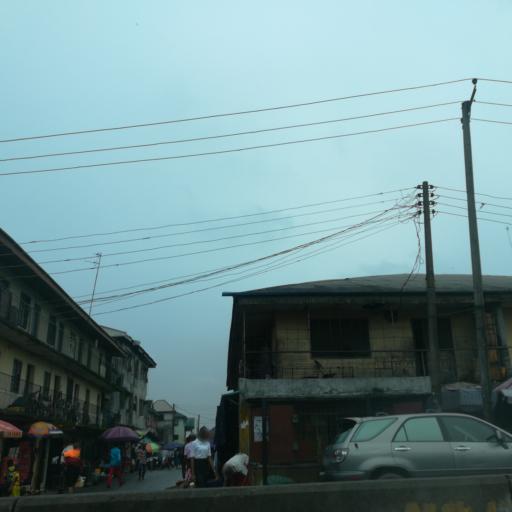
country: NG
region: Rivers
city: Port Harcourt
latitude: 4.8038
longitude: 6.9928
